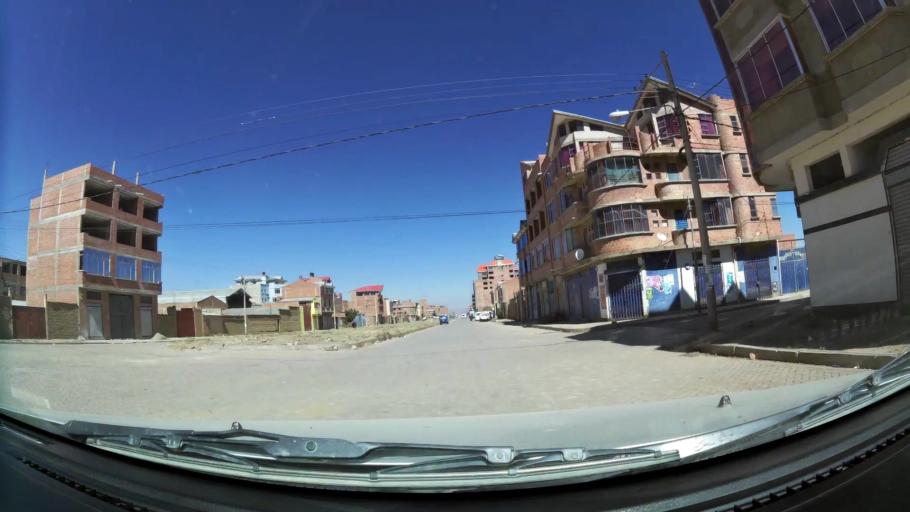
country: BO
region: La Paz
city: La Paz
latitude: -16.5393
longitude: -68.1963
